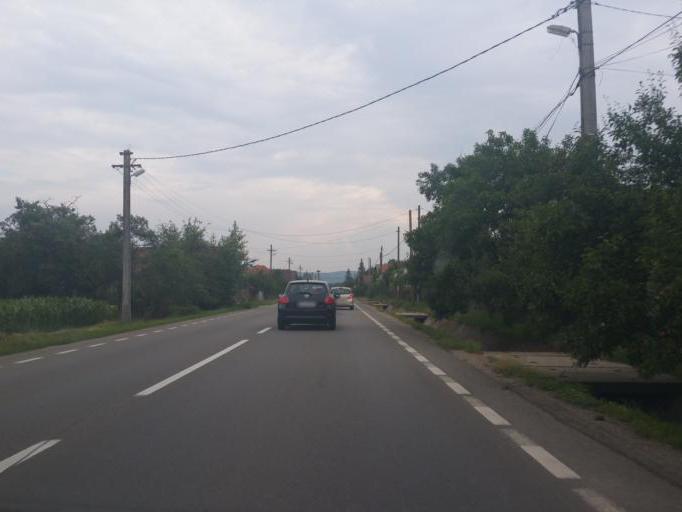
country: RO
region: Salaj
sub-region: Comuna Zimbor
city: Zimbor
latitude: 47.0090
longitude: 23.2617
